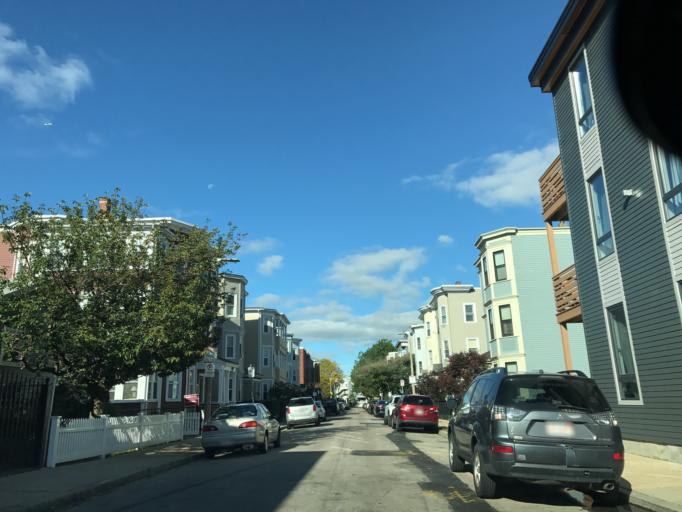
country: US
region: Massachusetts
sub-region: Suffolk County
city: South Boston
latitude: 42.3240
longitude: -71.0570
